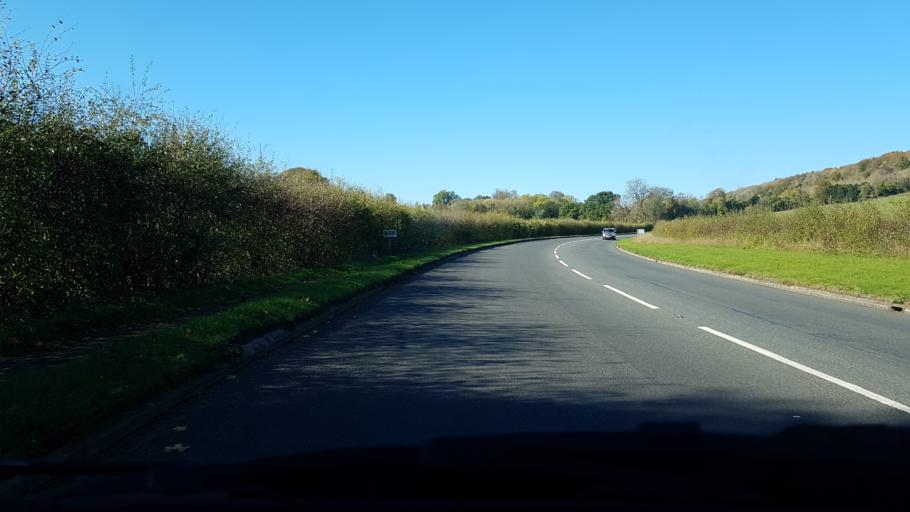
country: GB
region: England
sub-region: Surrey
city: East Horsley
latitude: 51.2209
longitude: -0.4588
